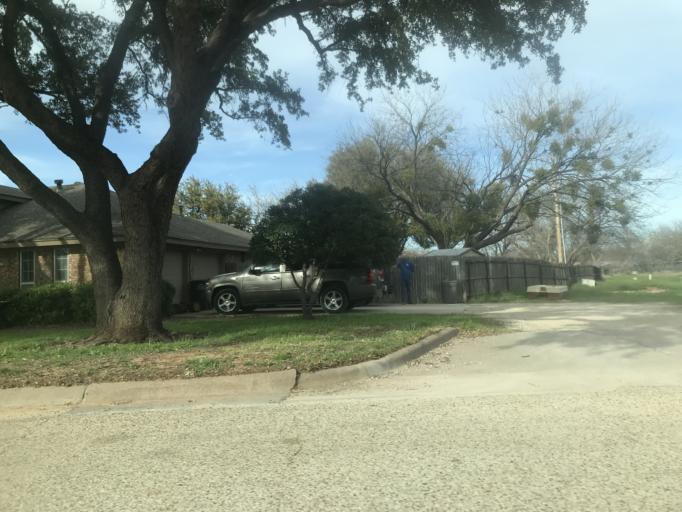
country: US
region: Texas
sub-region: Taylor County
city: Abilene
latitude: 32.4143
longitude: -99.7719
